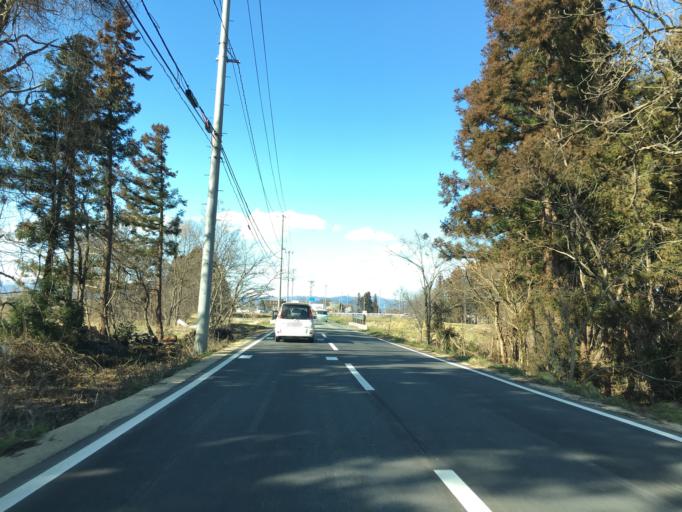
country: JP
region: Yamagata
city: Yonezawa
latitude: 37.9486
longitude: 140.1387
